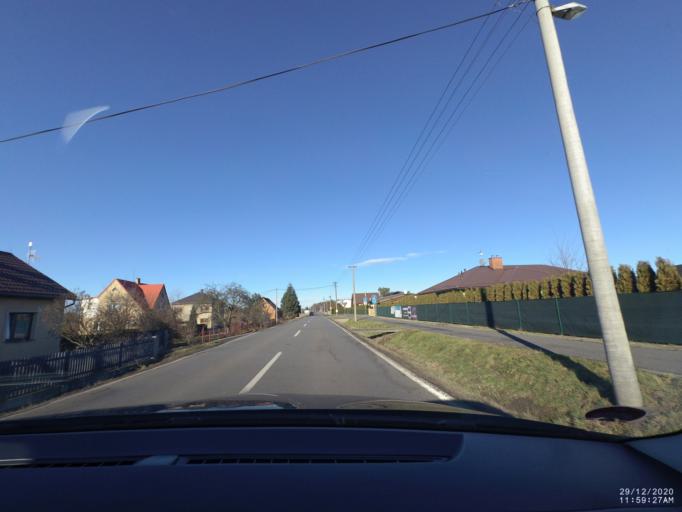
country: CZ
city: Sedliste
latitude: 49.7262
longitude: 18.3662
